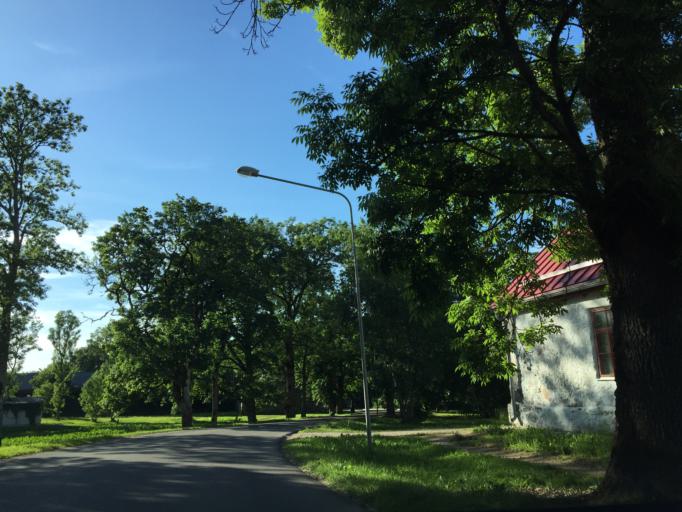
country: LV
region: Alsunga
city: Alsunga
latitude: 57.0159
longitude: 21.6967
